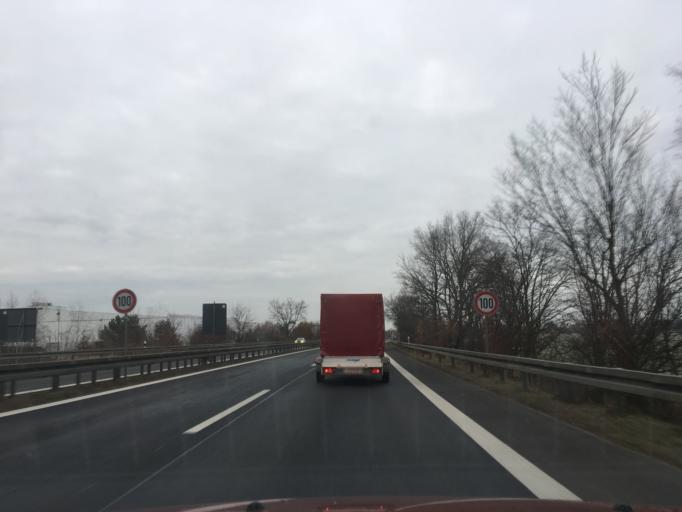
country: DE
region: Brandenburg
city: Schulzendorf
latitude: 52.3739
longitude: 13.5601
